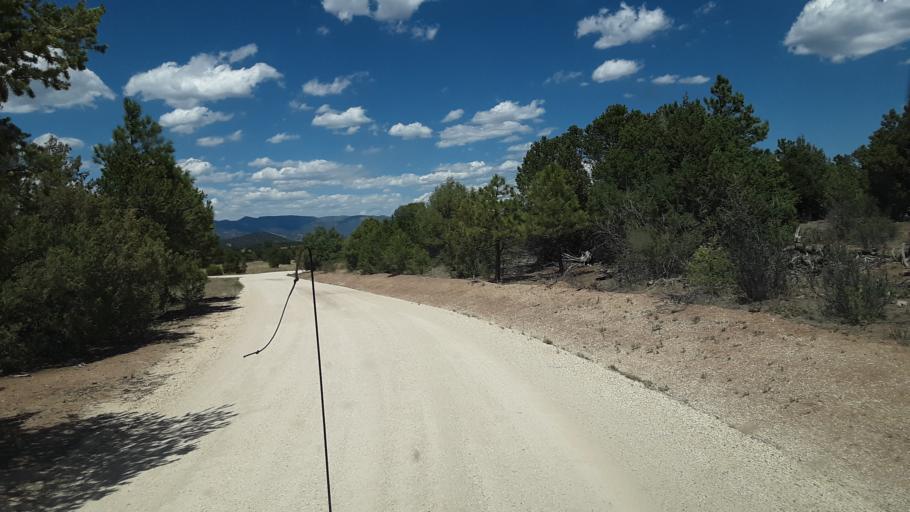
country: US
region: Colorado
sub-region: Custer County
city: Westcliffe
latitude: 38.3157
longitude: -105.6272
